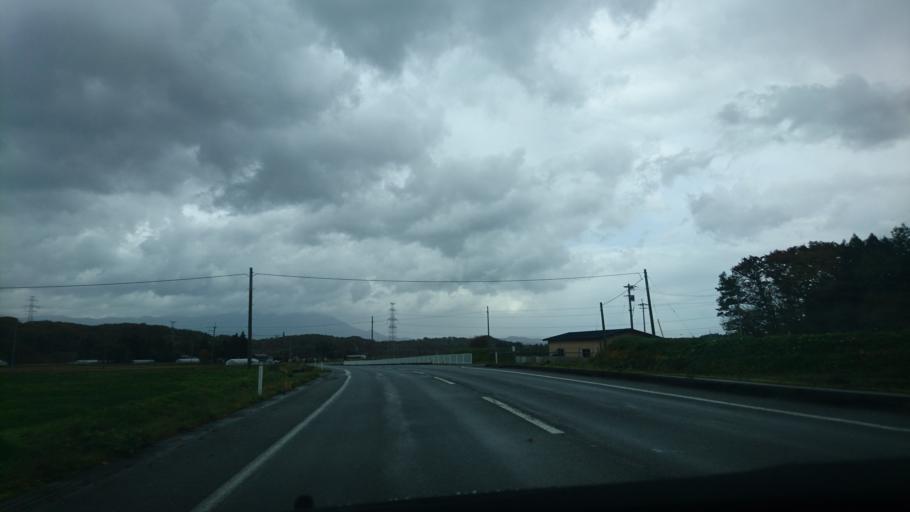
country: JP
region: Iwate
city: Shizukuishi
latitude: 39.6523
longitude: 140.9564
